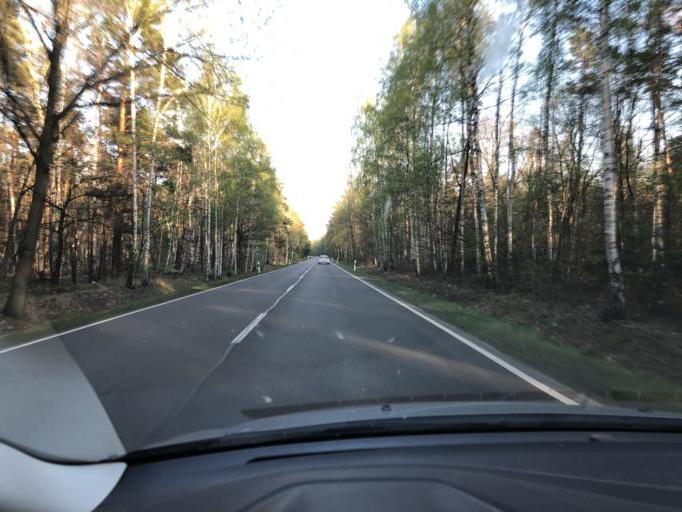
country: DE
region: Brandenburg
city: Welzow
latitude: 51.5494
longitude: 14.1548
